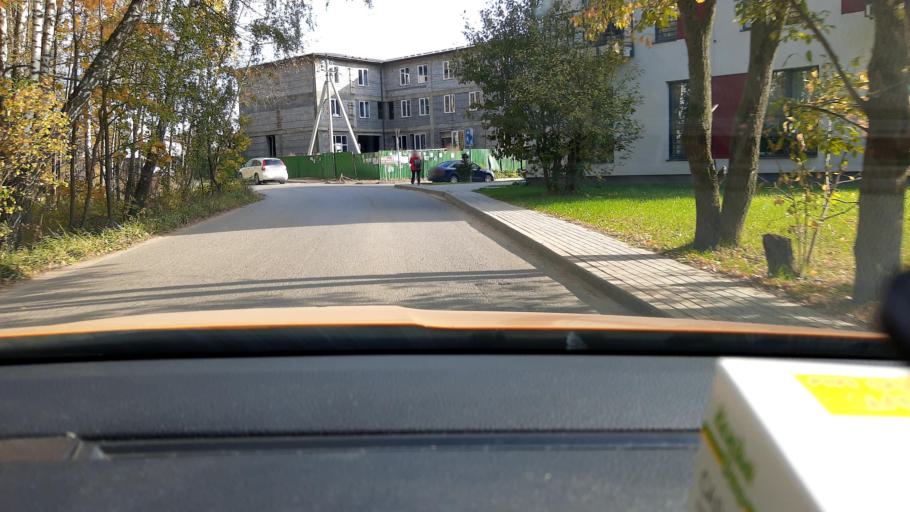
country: RU
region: Moskovskaya
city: Gorki-Leninskiye
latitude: 55.5243
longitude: 37.7972
